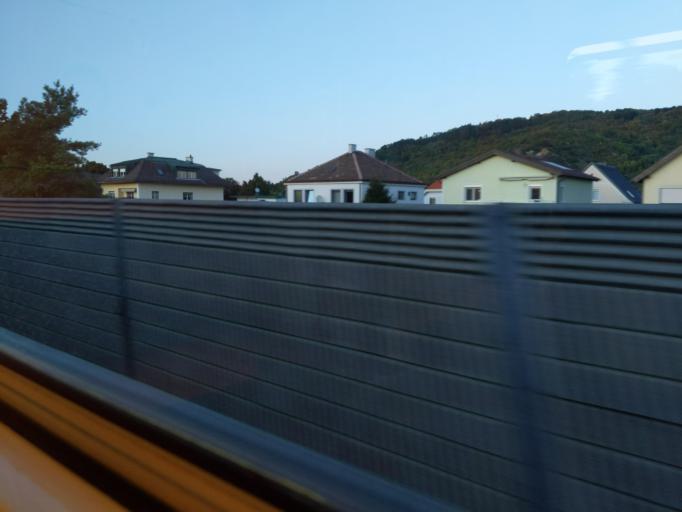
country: AT
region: Lower Austria
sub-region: Politischer Bezirk Korneuburg
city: Langenzersdorf
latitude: 48.3123
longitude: 16.3499
